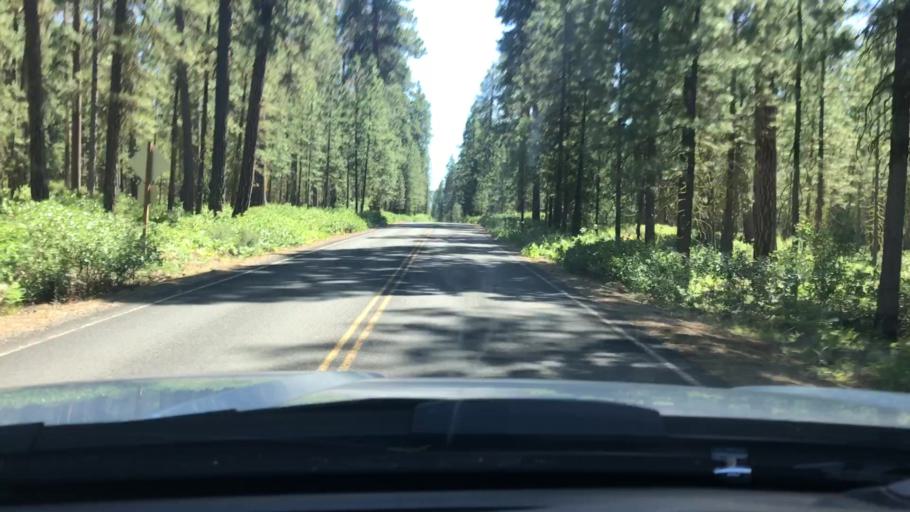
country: US
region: Oregon
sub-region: Deschutes County
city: Sisters
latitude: 44.4217
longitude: -121.6680
